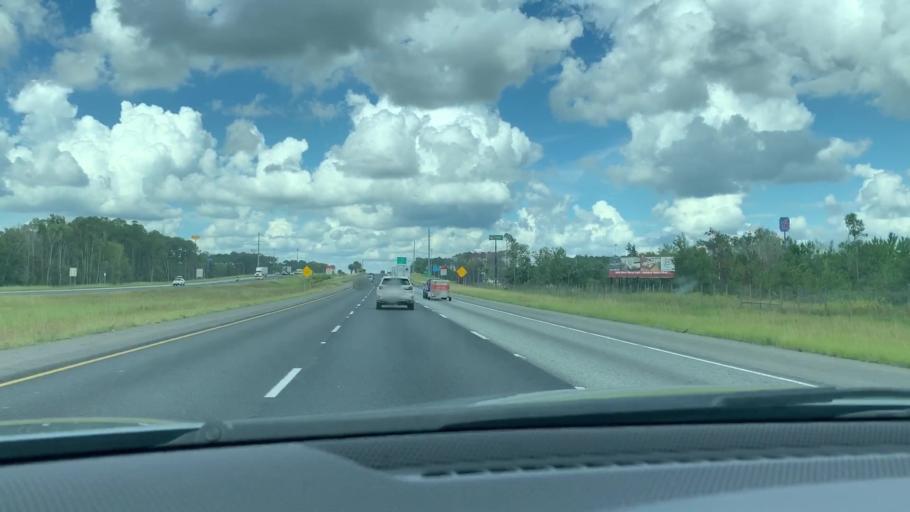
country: US
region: Georgia
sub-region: Camden County
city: Kingsland
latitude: 30.7855
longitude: -81.6576
